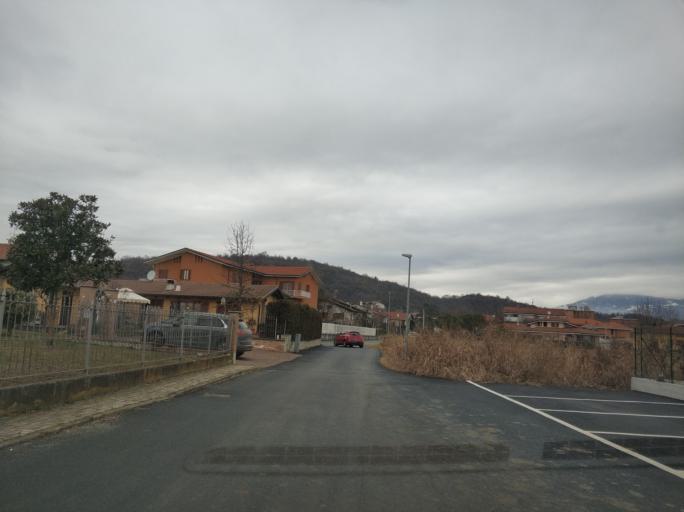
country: IT
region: Piedmont
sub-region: Provincia di Torino
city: Pavone Canavese
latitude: 45.4365
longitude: 7.8668
